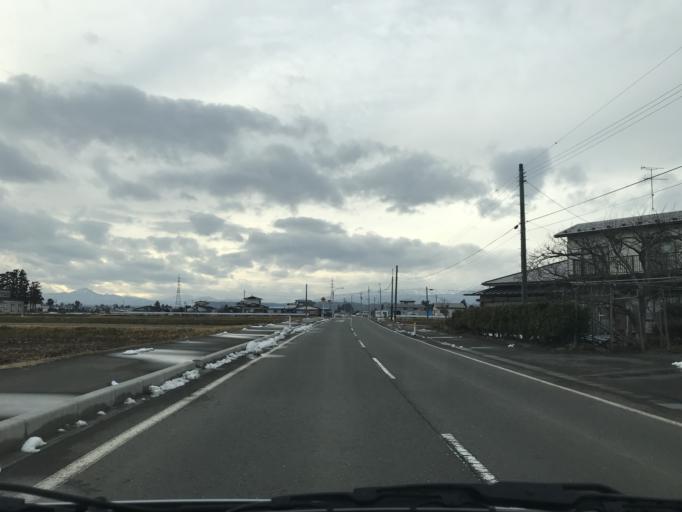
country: JP
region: Iwate
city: Mizusawa
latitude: 39.1545
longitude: 141.0907
